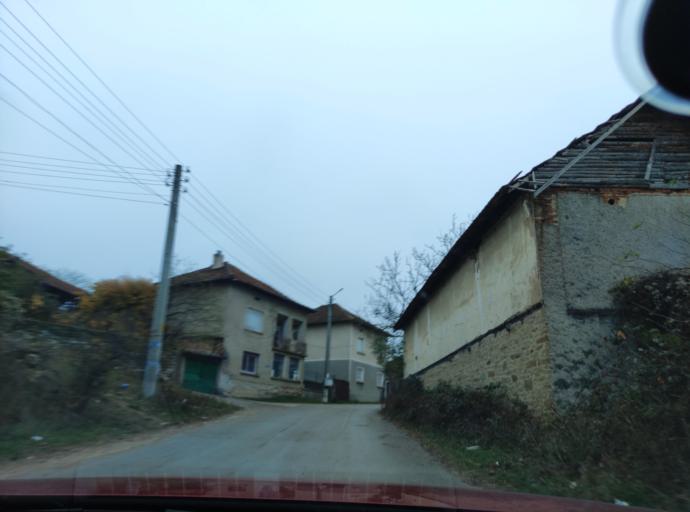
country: BG
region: Lovech
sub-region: Obshtina Yablanitsa
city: Yablanitsa
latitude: 43.1177
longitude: 24.0637
